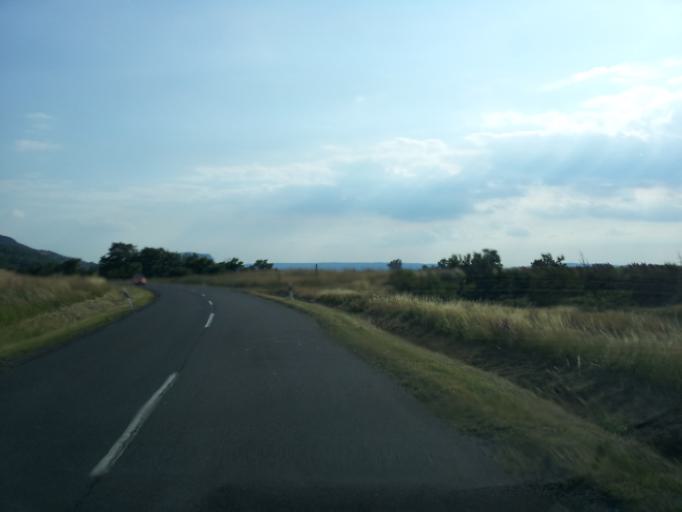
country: HU
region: Veszprem
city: Tapolca
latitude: 46.9029
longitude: 17.5242
